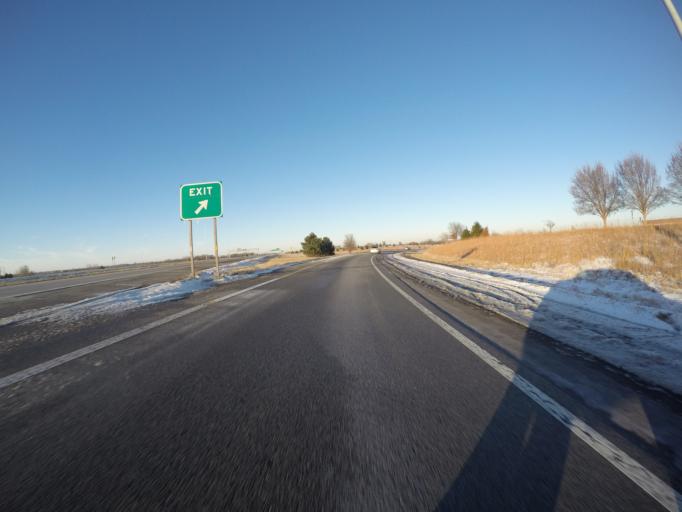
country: US
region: Kansas
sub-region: Johnson County
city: Olathe
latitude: 38.9379
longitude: -94.8524
